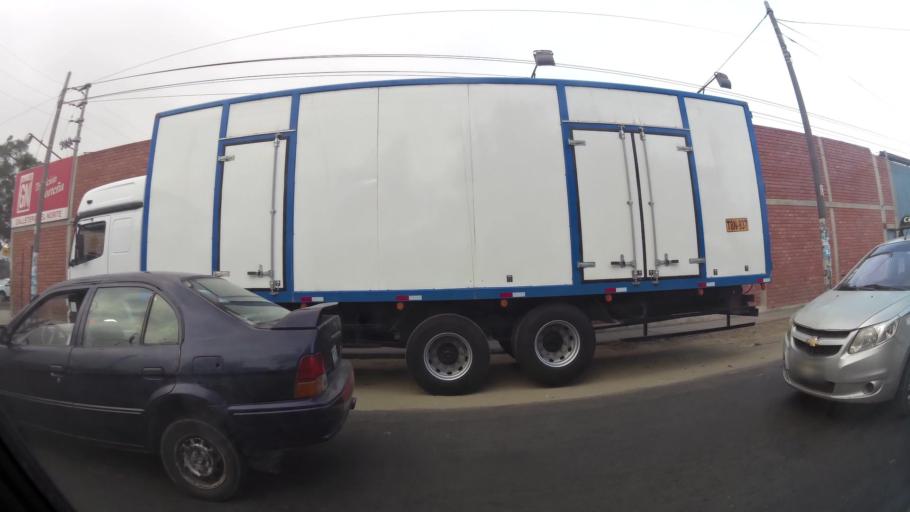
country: PE
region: La Libertad
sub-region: Provincia de Trujillo
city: Trujillo
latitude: -8.0950
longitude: -79.0321
